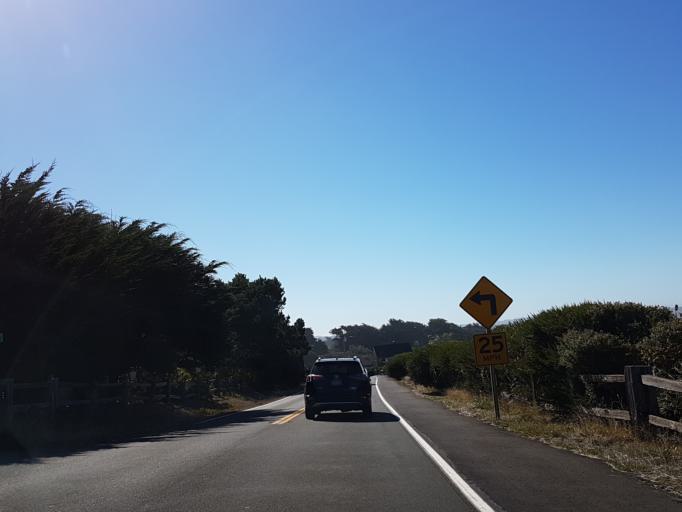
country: US
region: California
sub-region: Mendocino County
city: Boonville
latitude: 39.0228
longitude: -123.6881
